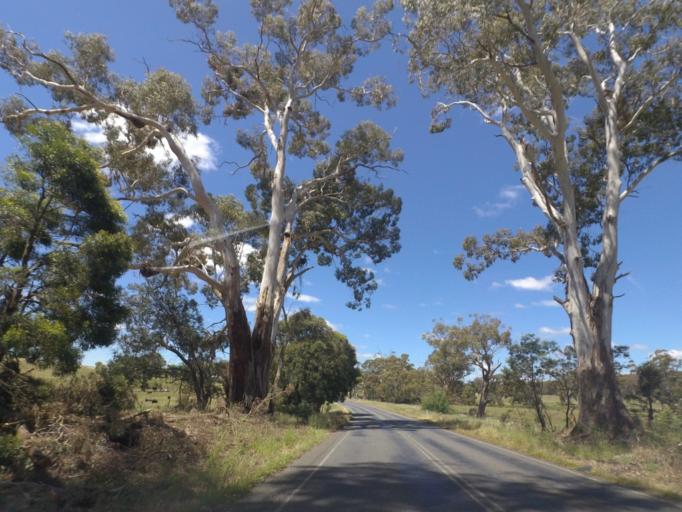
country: AU
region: Victoria
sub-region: Mount Alexander
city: Castlemaine
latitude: -37.3151
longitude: 144.2235
